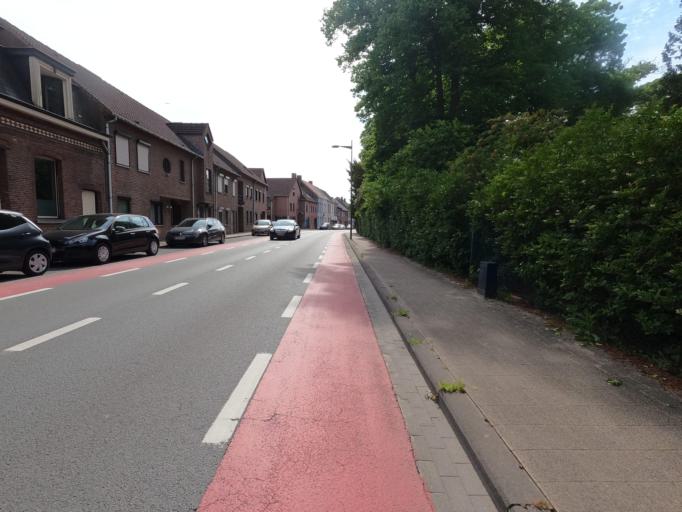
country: BE
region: Flanders
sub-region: Provincie Antwerpen
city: Essen
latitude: 51.4631
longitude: 4.4542
